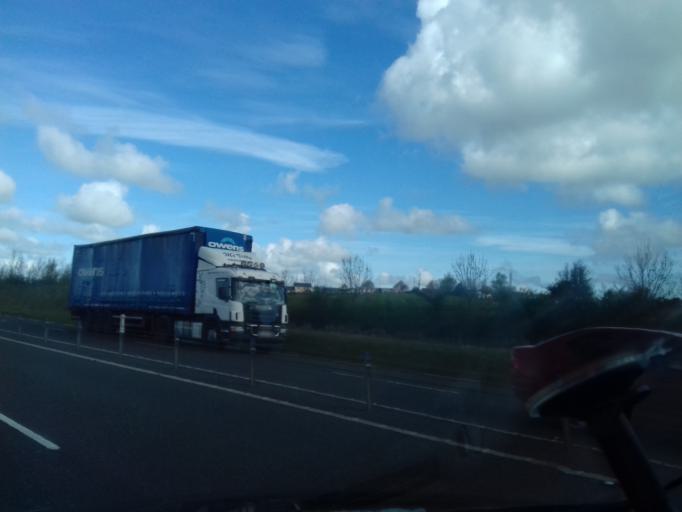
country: IE
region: Leinster
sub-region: An Mhi
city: Kells
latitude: 53.7219
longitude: -6.9416
